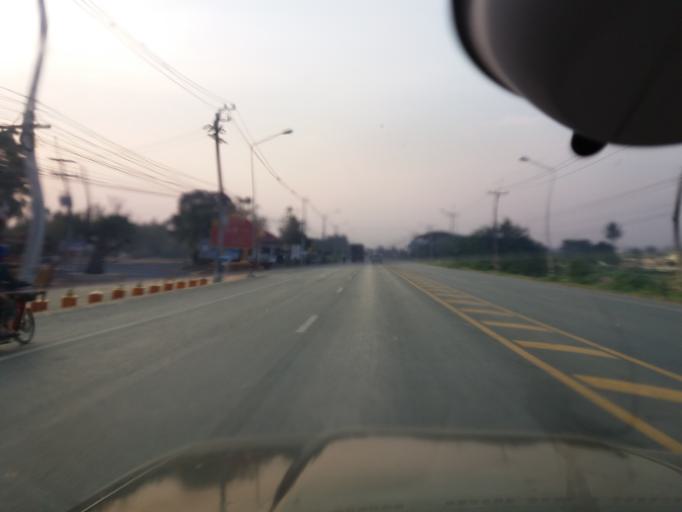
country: TH
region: Sing Buri
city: Sing Buri
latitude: 14.8847
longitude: 100.3776
